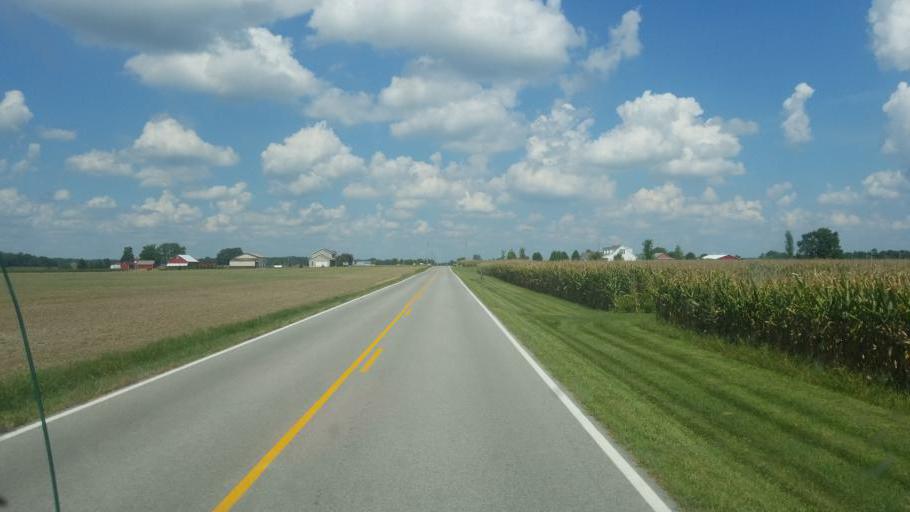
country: US
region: Ohio
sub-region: Hancock County
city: Arlington
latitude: 40.8714
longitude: -83.7272
